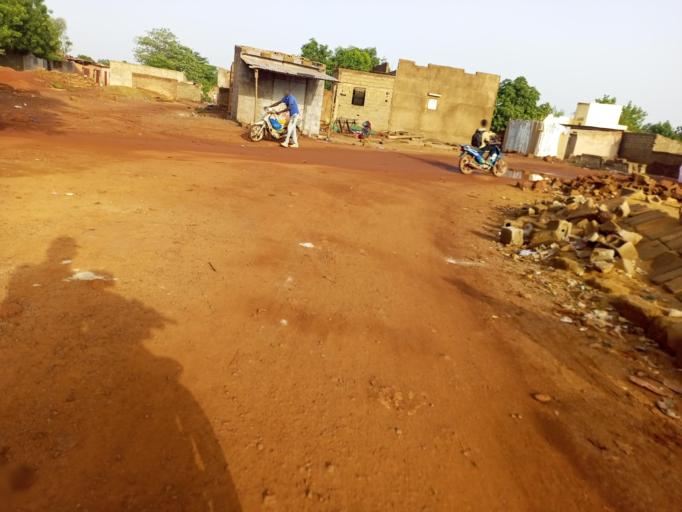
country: ML
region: Bamako
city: Bamako
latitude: 12.5203
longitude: -7.9932
